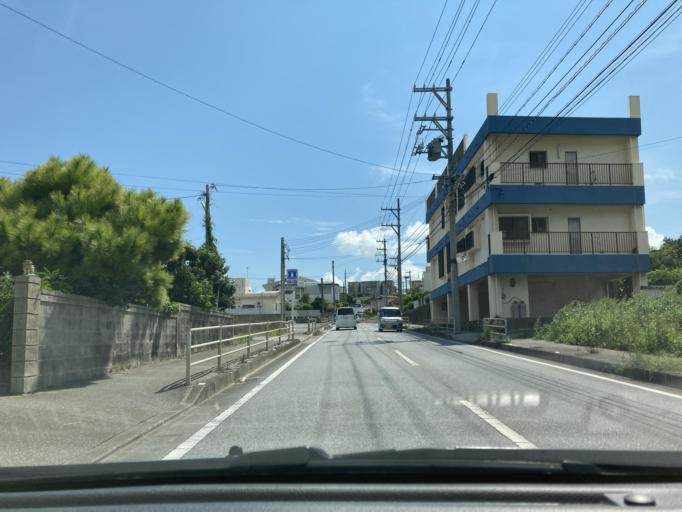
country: JP
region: Okinawa
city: Tomigusuku
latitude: 26.1813
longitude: 127.7412
